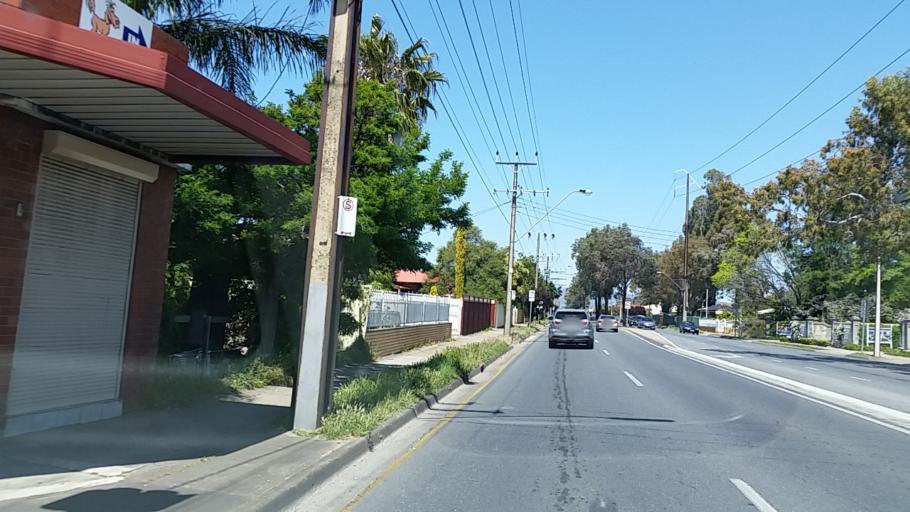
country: AU
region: South Australia
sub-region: Charles Sturt
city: Woodville North
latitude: -34.8722
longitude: 138.5436
